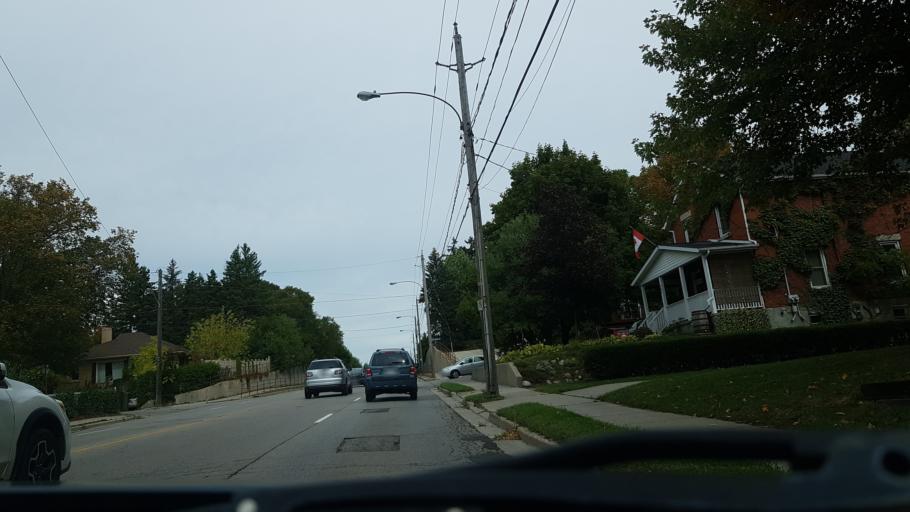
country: CA
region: Ontario
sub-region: Wellington County
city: Guelph
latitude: 43.5648
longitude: -80.2483
